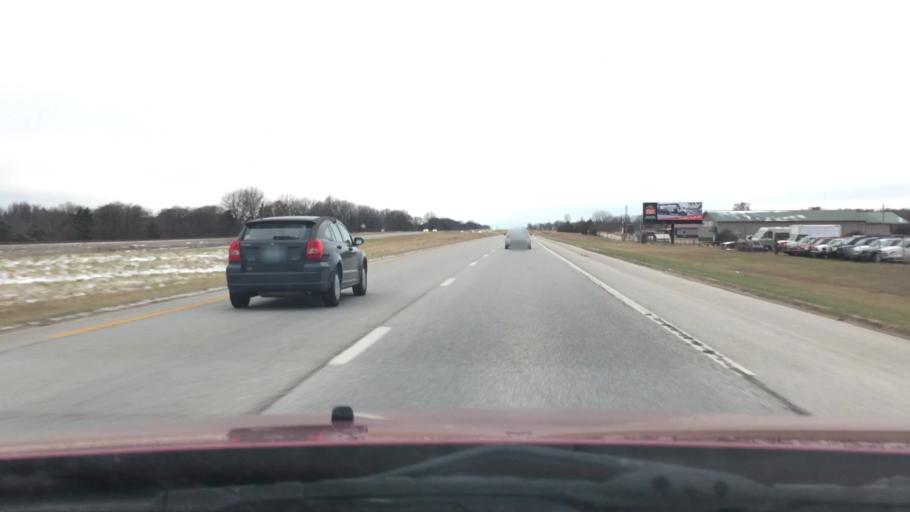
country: US
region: Missouri
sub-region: Webster County
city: Seymour
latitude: 37.1696
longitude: -92.8269
